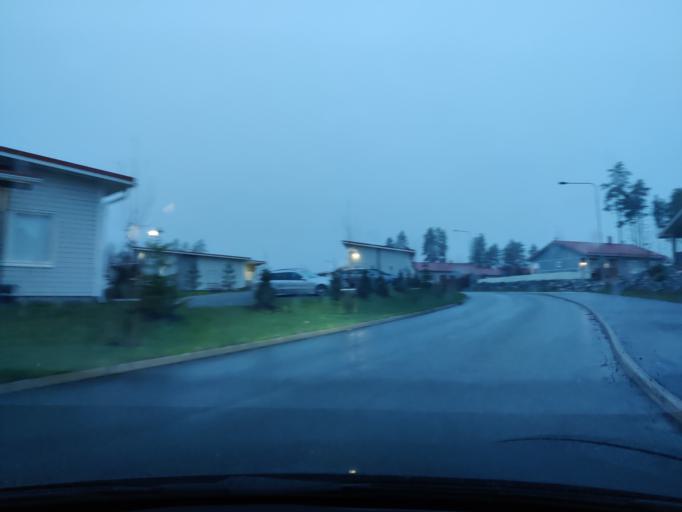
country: FI
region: Northern Savo
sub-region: Kuopio
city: Kuopio
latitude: 62.8272
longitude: 27.7204
